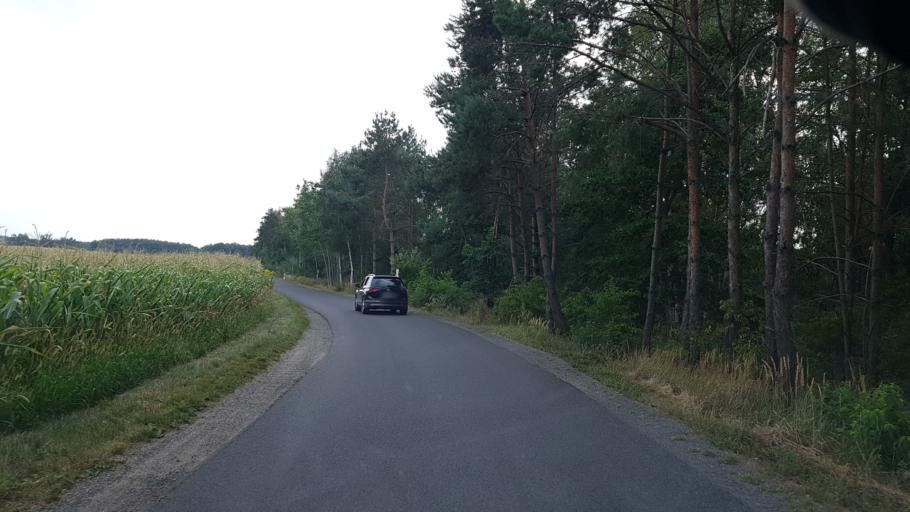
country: DE
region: Brandenburg
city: Plessa
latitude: 51.5142
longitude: 13.6800
